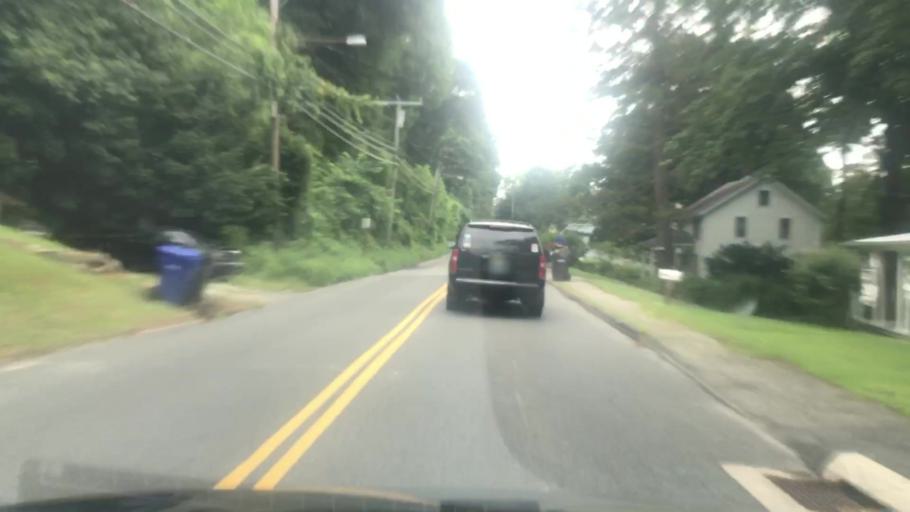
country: US
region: Connecticut
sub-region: Litchfield County
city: New Milford
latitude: 41.5854
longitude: -73.4186
